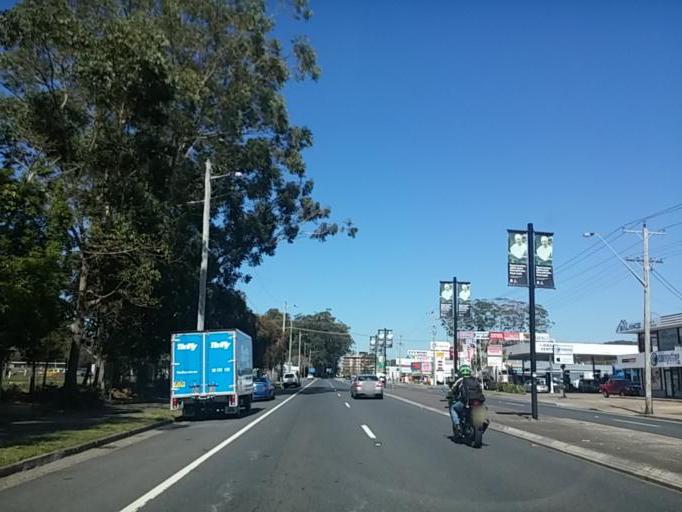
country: AU
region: New South Wales
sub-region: Coffs Harbour
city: Coffs Harbour
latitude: -30.2905
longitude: 153.1206
